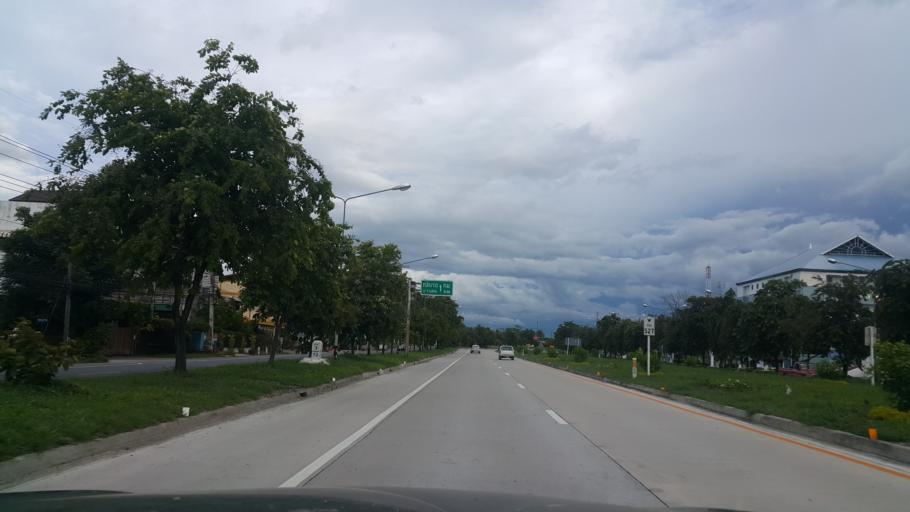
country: TH
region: Tak
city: Tak
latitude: 16.9027
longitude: 99.1258
